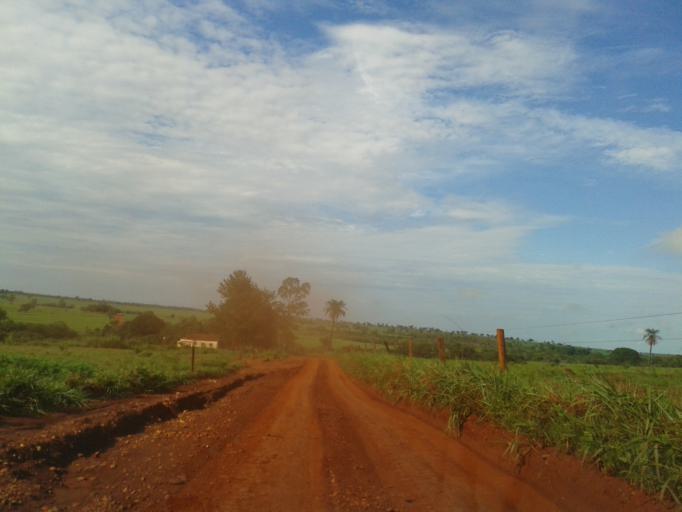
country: BR
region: Minas Gerais
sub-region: Santa Vitoria
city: Santa Vitoria
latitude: -19.2158
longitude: -50.6736
